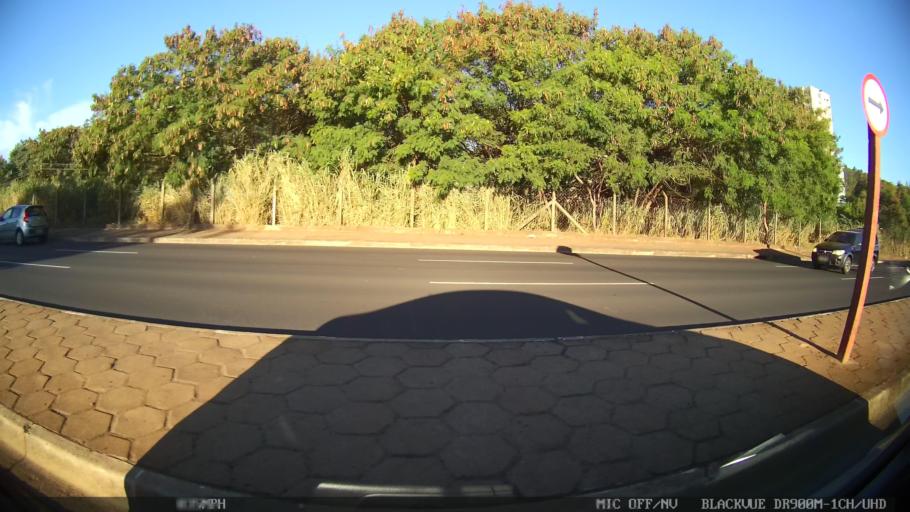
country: BR
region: Sao Paulo
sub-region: Araraquara
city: Araraquara
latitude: -21.7748
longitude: -48.1673
